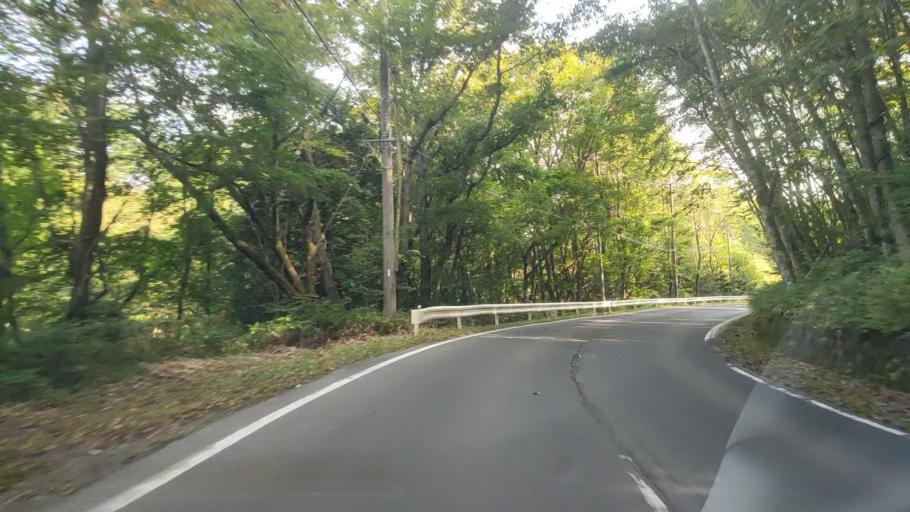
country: JP
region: Nagano
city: Suzaka
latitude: 36.5690
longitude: 138.5563
